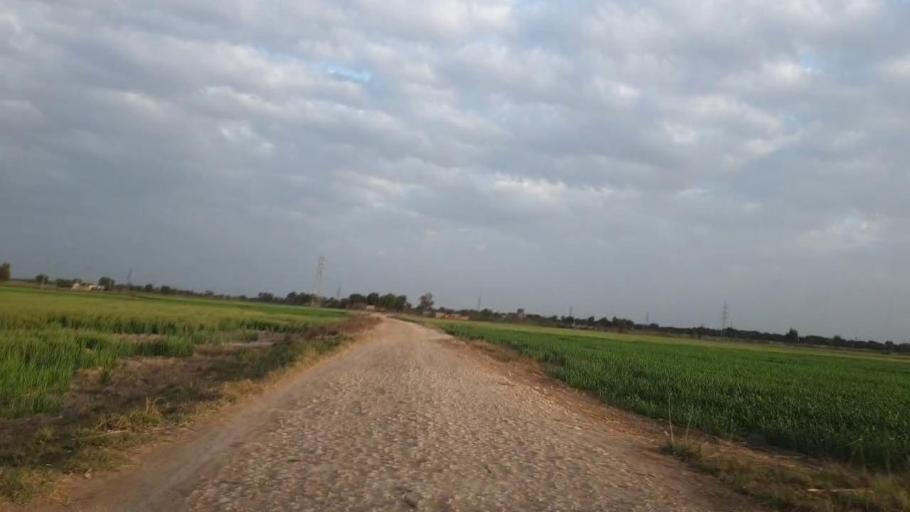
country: PK
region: Sindh
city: Matiari
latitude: 25.5679
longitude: 68.4430
